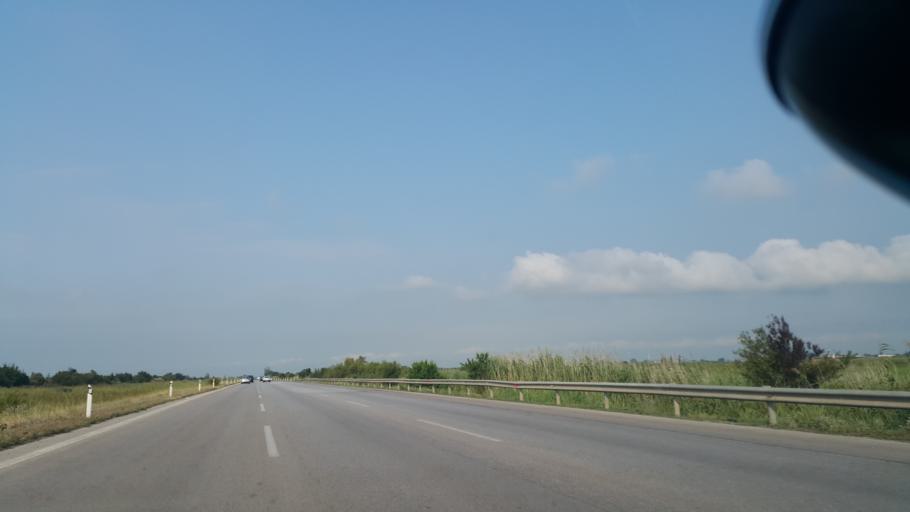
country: GR
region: Central Macedonia
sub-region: Nomos Thessalonikis
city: Sindos
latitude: 40.6342
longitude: 22.7819
